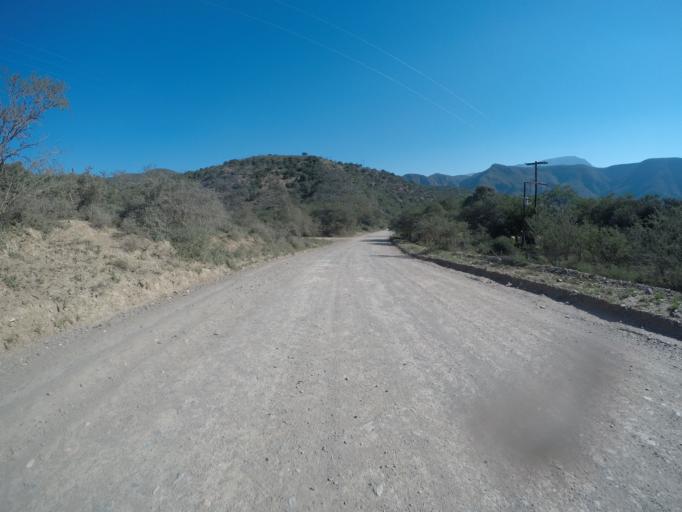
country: ZA
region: Eastern Cape
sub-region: Cacadu District Municipality
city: Kruisfontein
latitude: -33.6703
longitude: 24.5700
